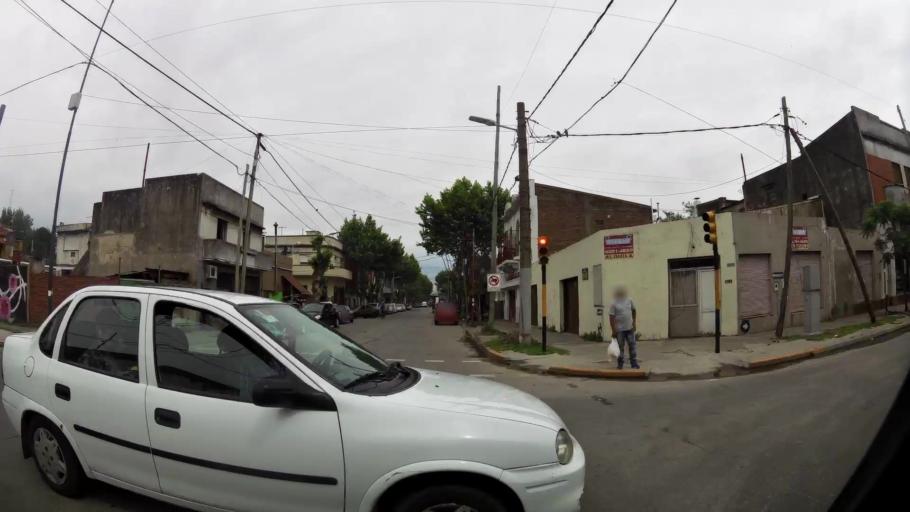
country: AR
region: Buenos Aires
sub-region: Partido de Avellaneda
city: Avellaneda
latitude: -34.6553
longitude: -58.3436
